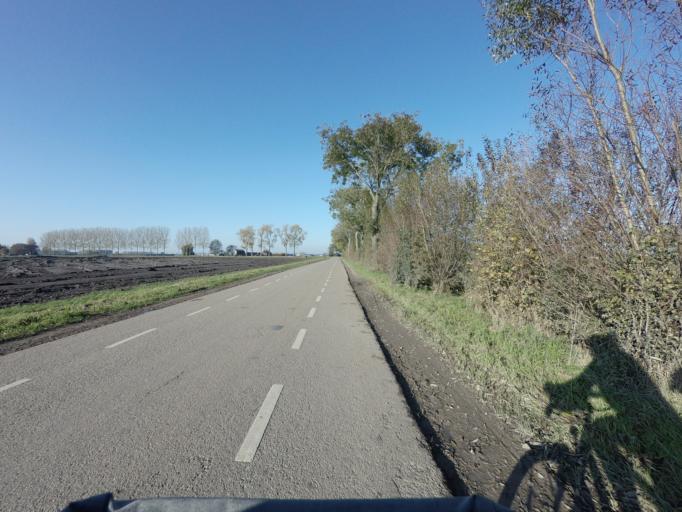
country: NL
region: North Brabant
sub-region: Gemeente Woudrichem
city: Woudrichem
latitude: 51.7659
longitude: 5.0496
